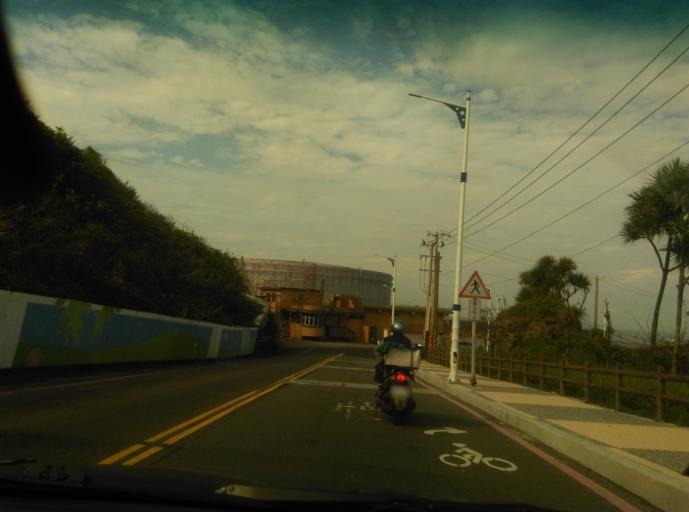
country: TW
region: Taiwan
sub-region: Keelung
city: Keelung
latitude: 25.1596
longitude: 121.7323
